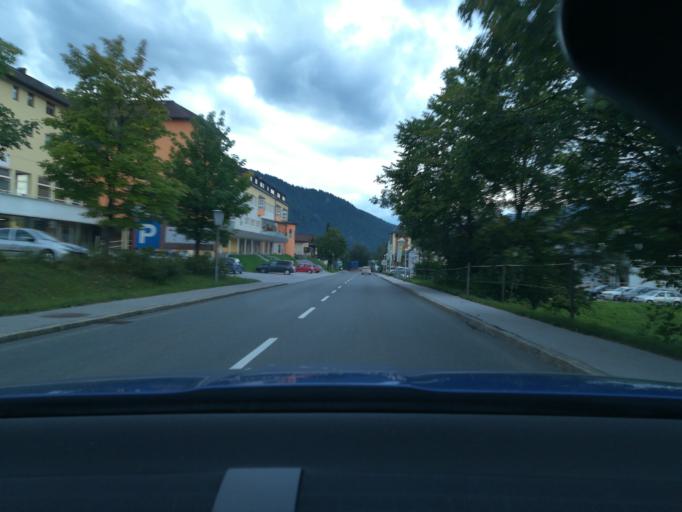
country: AT
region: Salzburg
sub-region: Politischer Bezirk Hallein
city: Abtenau
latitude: 47.5673
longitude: 13.3394
